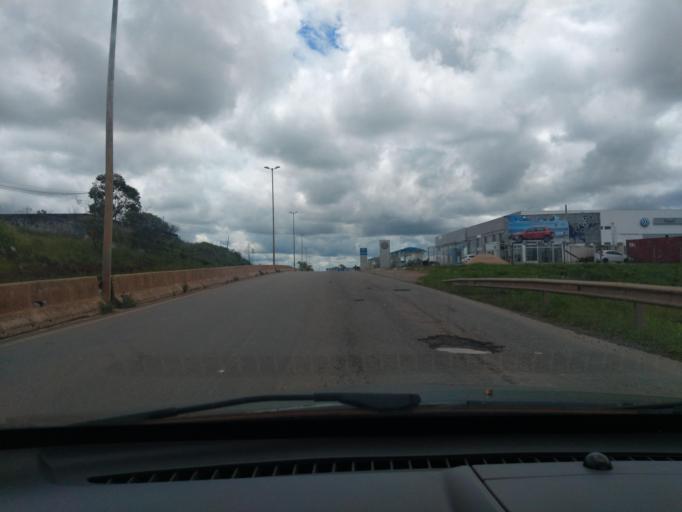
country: BR
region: Minas Gerais
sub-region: Lavras
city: Lavras
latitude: -21.2352
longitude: -45.0306
